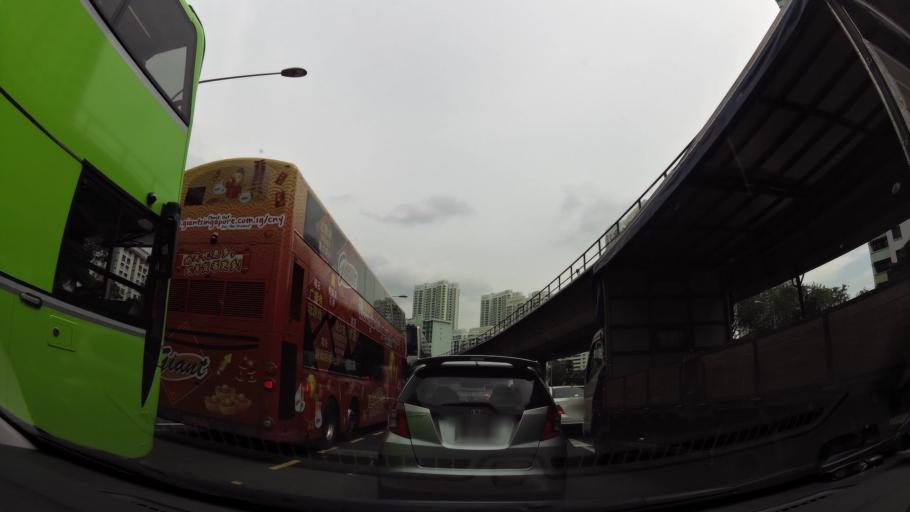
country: SG
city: Singapore
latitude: 1.3124
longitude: 103.7674
